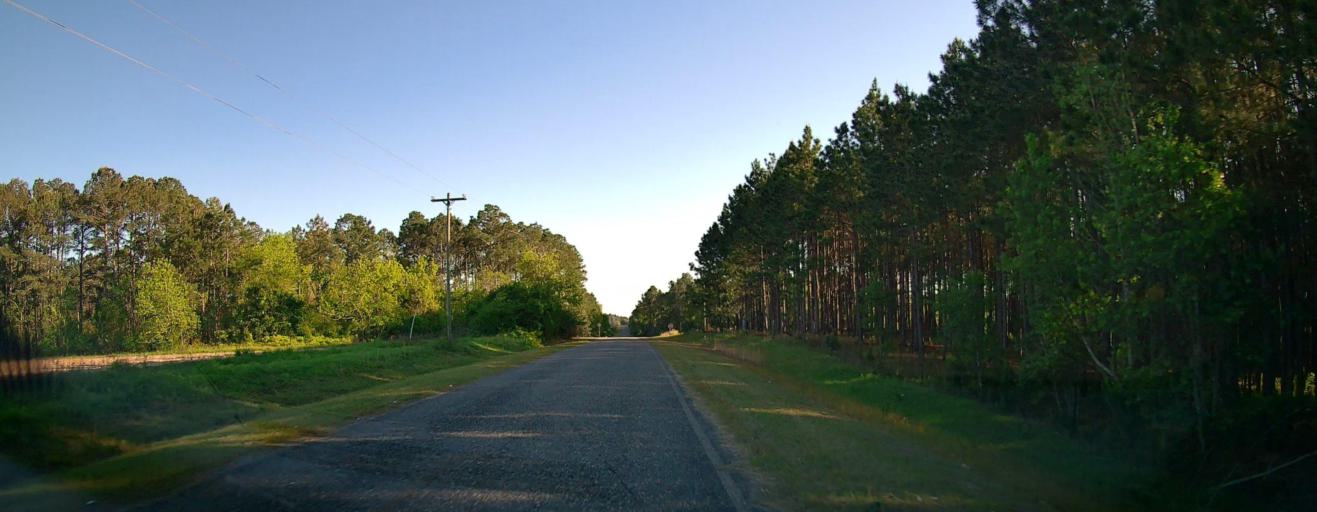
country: US
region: Georgia
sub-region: Ben Hill County
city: Fitzgerald
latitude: 31.6602
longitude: -83.1470
